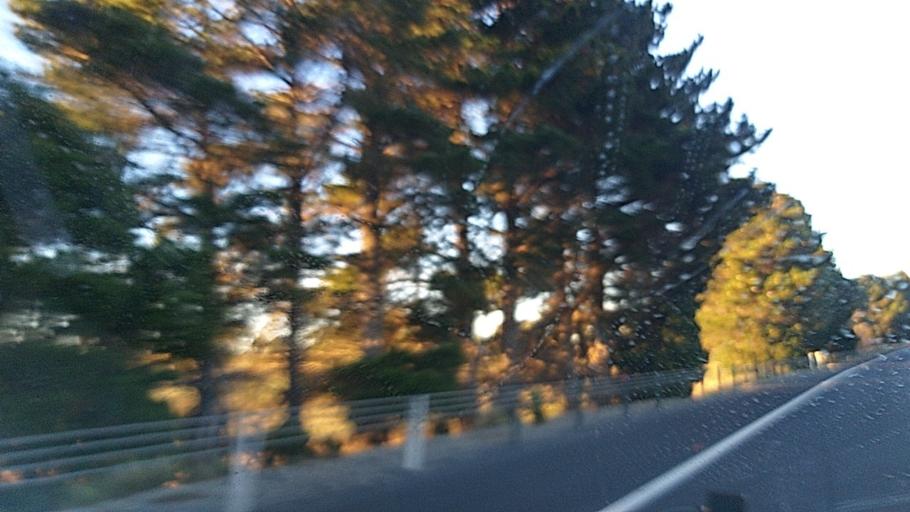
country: AU
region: New South Wales
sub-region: Goulburn Mulwaree
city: Goulburn
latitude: -34.8907
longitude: 149.5276
